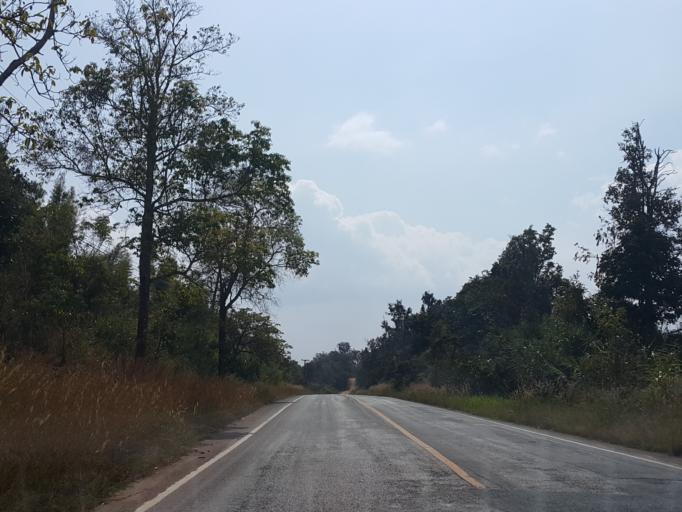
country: TH
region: Chiang Mai
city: Hot
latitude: 18.0978
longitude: 98.3751
